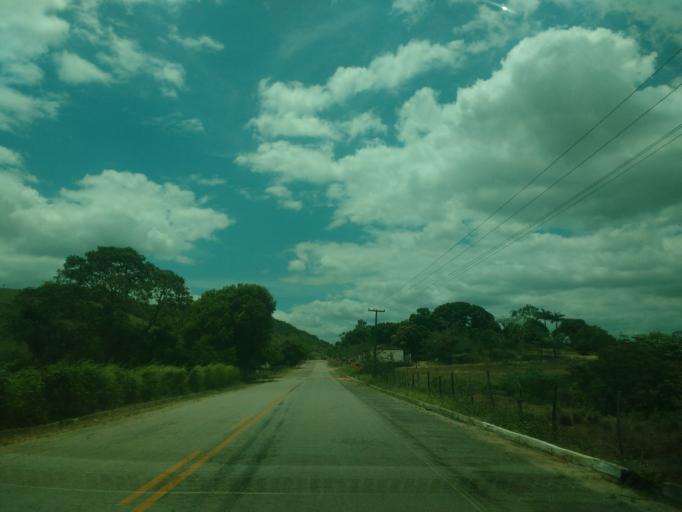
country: BR
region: Alagoas
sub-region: Uniao Dos Palmares
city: Uniao dos Palmares
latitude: -9.1425
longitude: -36.0814
